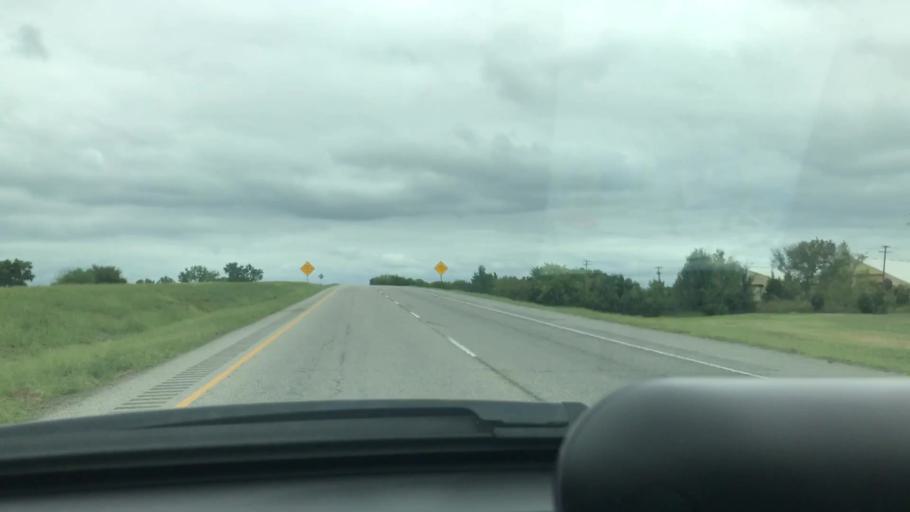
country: US
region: Oklahoma
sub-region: Wagoner County
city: Wagoner
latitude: 35.9771
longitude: -95.3828
